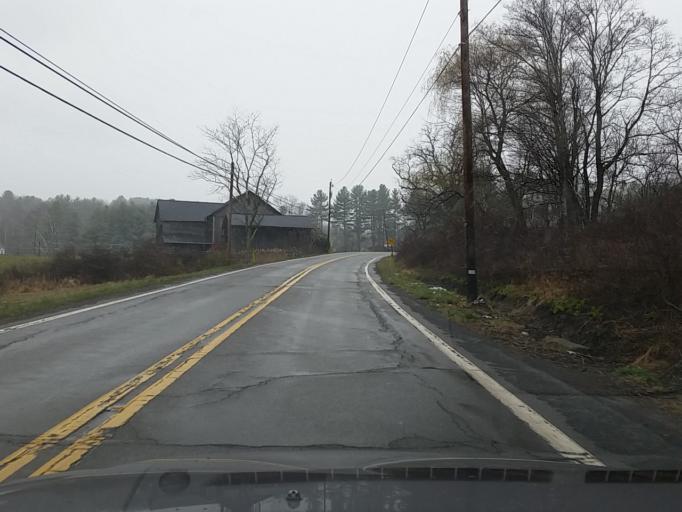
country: US
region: Pennsylvania
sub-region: Luzerne County
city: East Berwick
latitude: 41.1909
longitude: -76.2768
